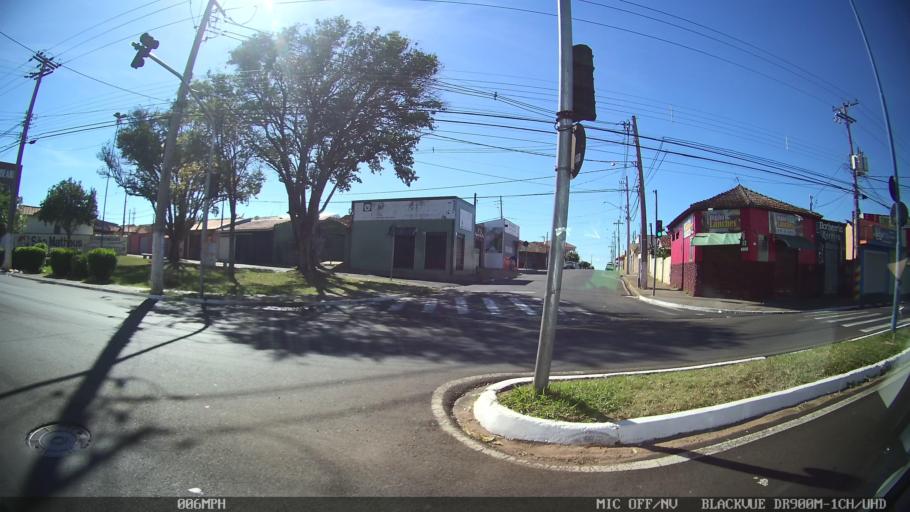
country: BR
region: Sao Paulo
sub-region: Franca
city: Franca
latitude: -20.5304
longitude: -47.3676
